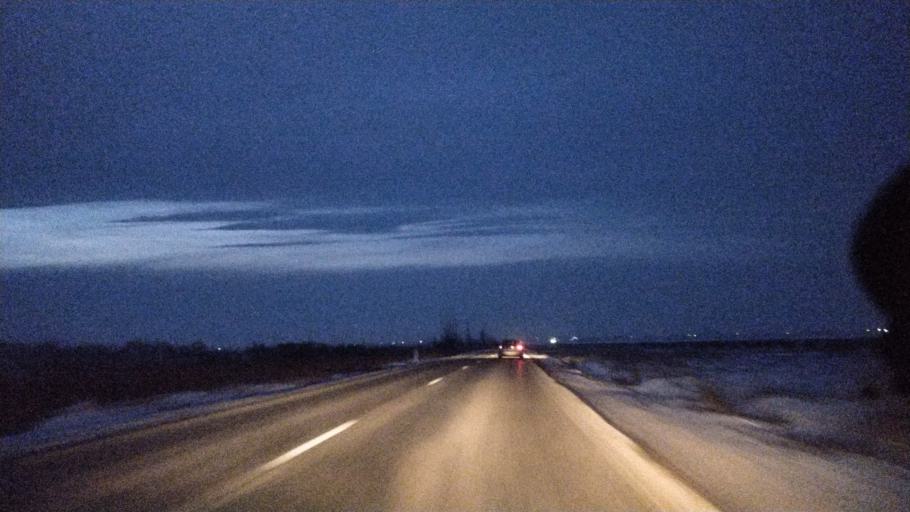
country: RO
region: Vrancea
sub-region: Comuna Milcovul
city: Milcovul
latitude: 45.6701
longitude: 27.2612
